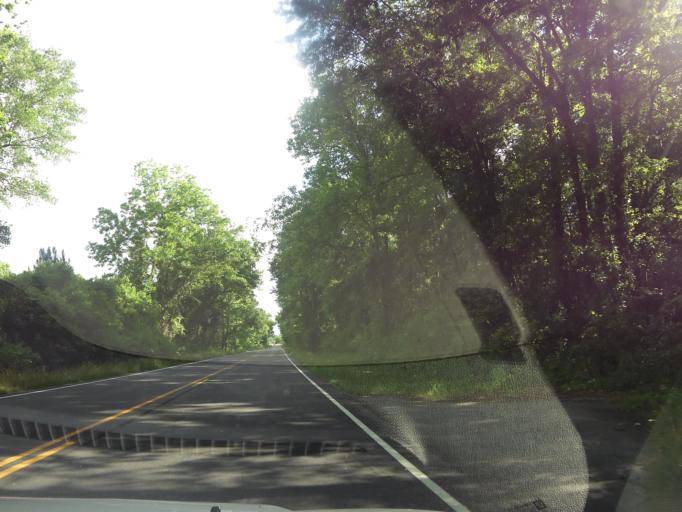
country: US
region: South Carolina
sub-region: Allendale County
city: Fairfax
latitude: 32.9481
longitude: -81.2361
